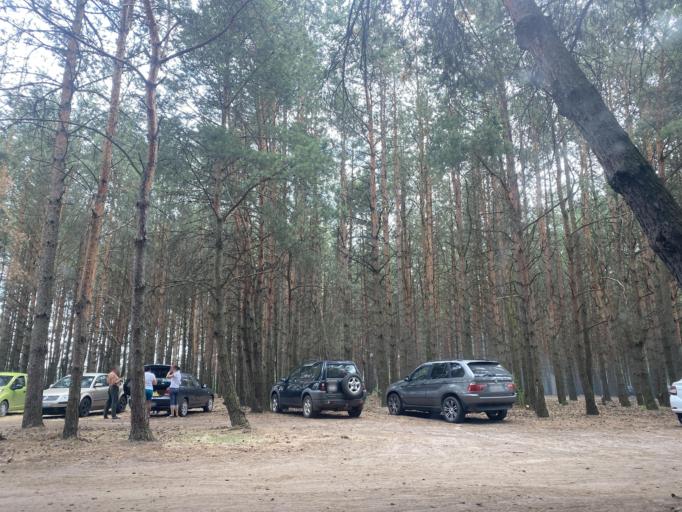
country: BY
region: Brest
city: Ivanava
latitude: 52.3666
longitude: 25.6323
